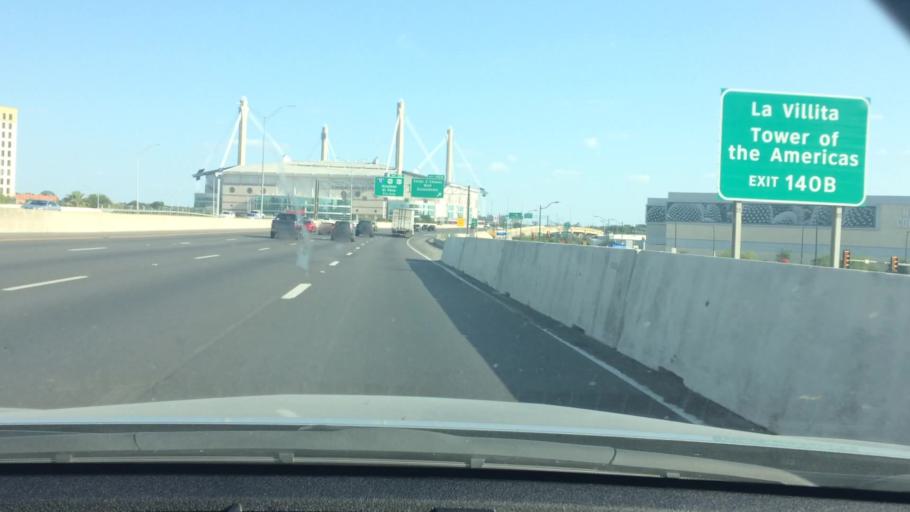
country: US
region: Texas
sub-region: Bexar County
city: San Antonio
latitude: 29.4228
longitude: -98.4811
